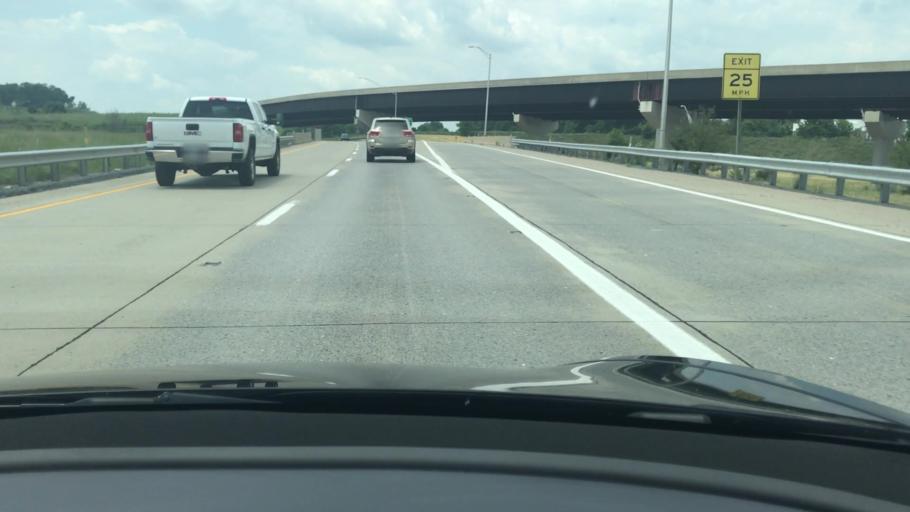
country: US
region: Pennsylvania
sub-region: Centre County
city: Houserville
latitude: 40.8250
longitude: -77.8439
